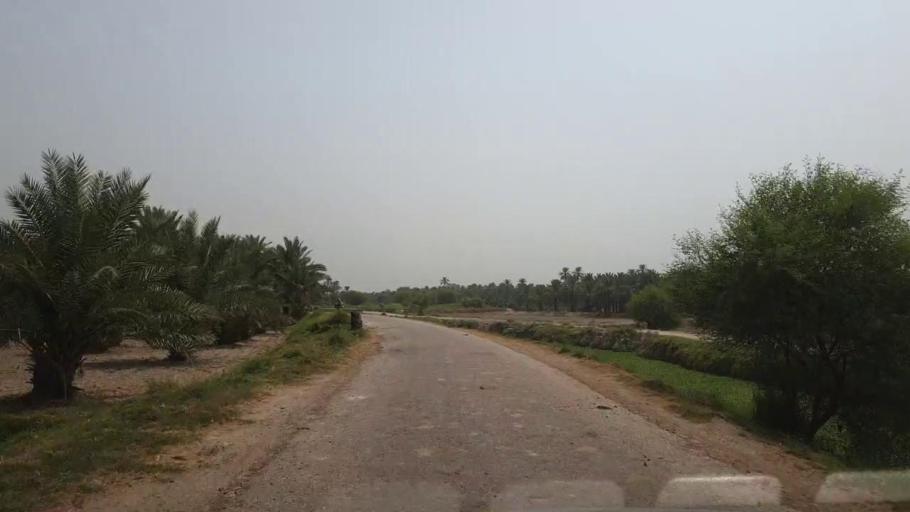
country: PK
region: Sindh
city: Gambat
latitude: 27.4250
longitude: 68.5589
